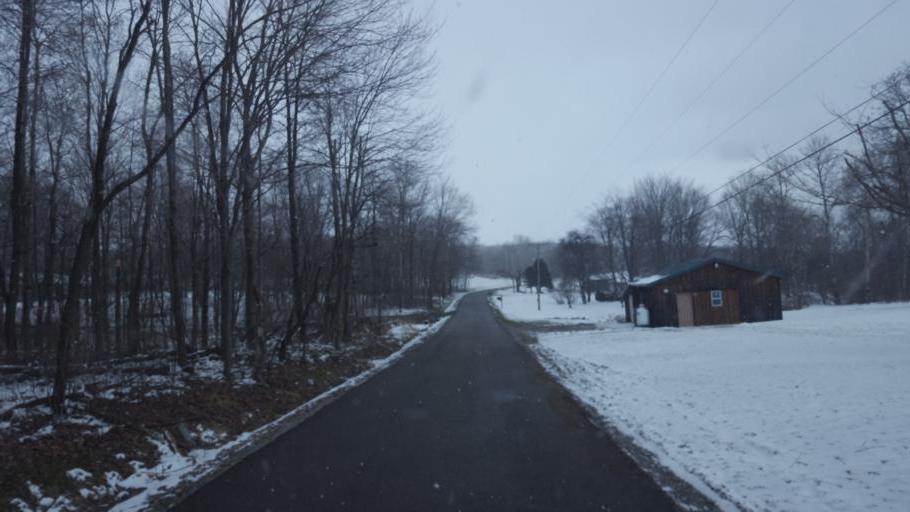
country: US
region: Pennsylvania
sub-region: Mercer County
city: Stoneboro
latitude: 41.4247
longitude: -80.0746
